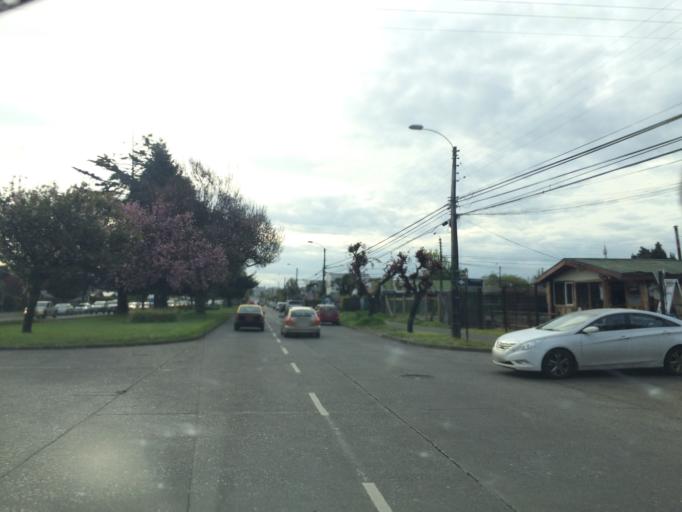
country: CL
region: Araucania
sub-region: Provincia de Cautin
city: Temuco
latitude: -38.7389
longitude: -72.6268
